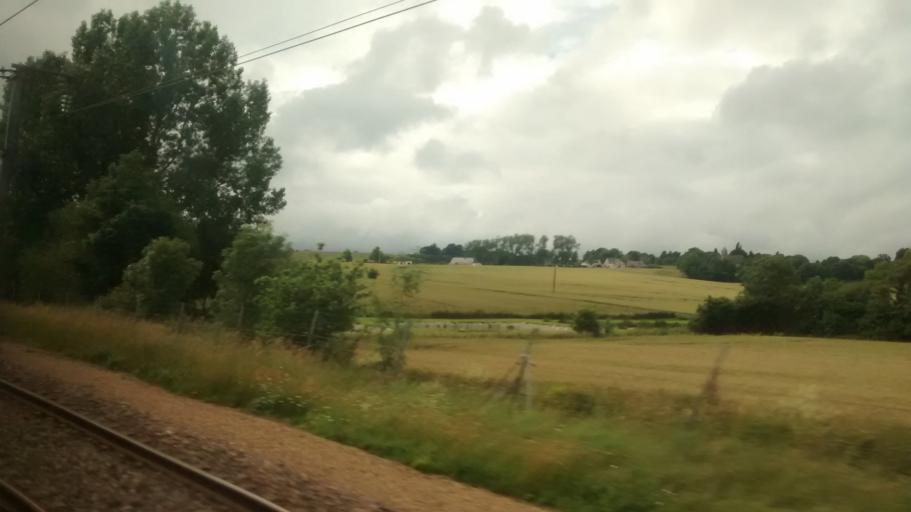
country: FR
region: Centre
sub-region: Departement d'Eure-et-Loir
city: La Bazoche-Gouet
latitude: 48.0837
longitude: 0.9198
